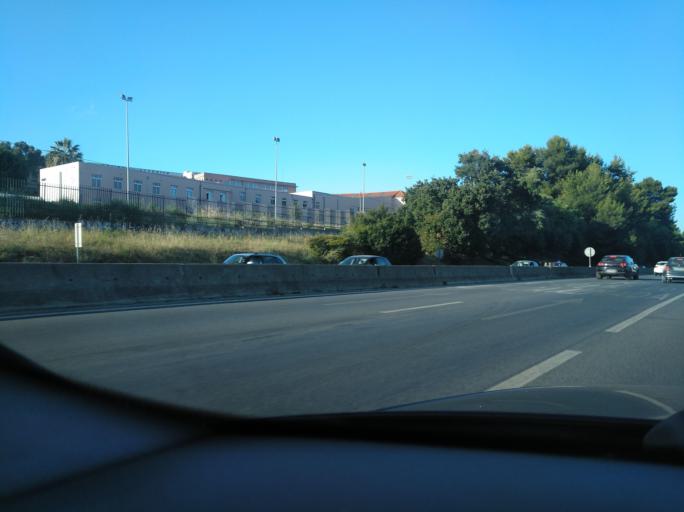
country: PT
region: Setubal
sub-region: Almada
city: Pragal
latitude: 38.6648
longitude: -9.1771
